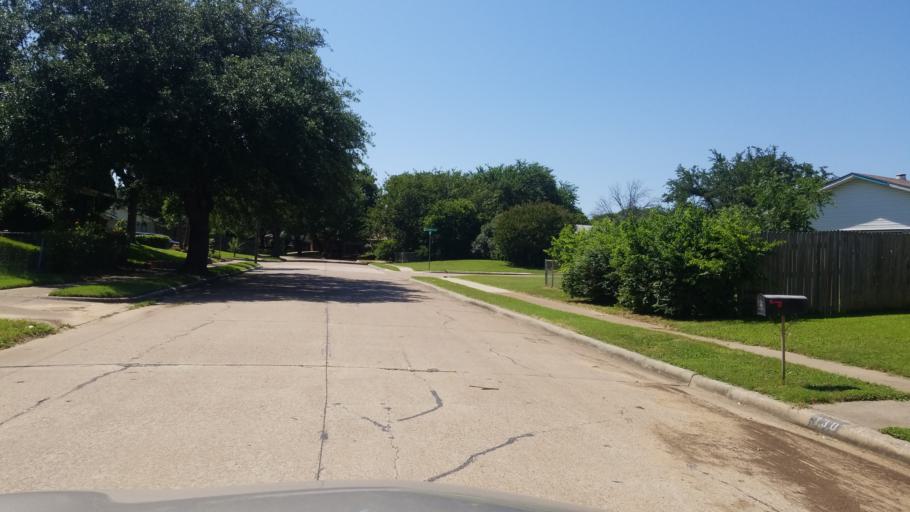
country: US
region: Texas
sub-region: Dallas County
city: Grand Prairie
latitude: 32.6918
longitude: -96.9957
